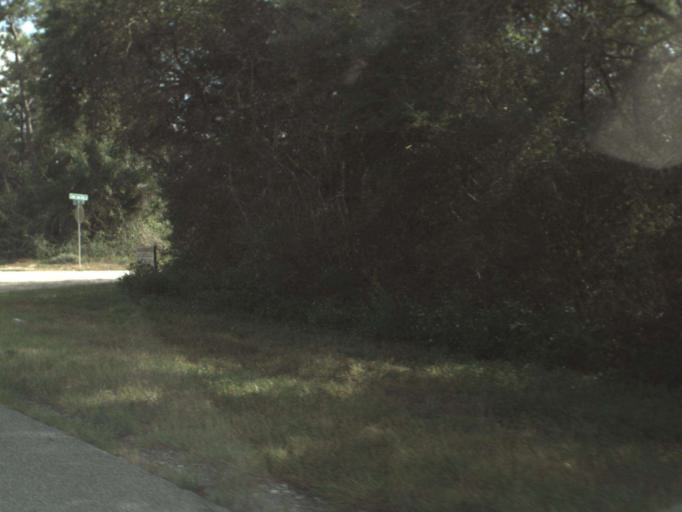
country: US
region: Florida
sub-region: Bay County
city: Mexico Beach
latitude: 29.9655
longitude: -85.4481
